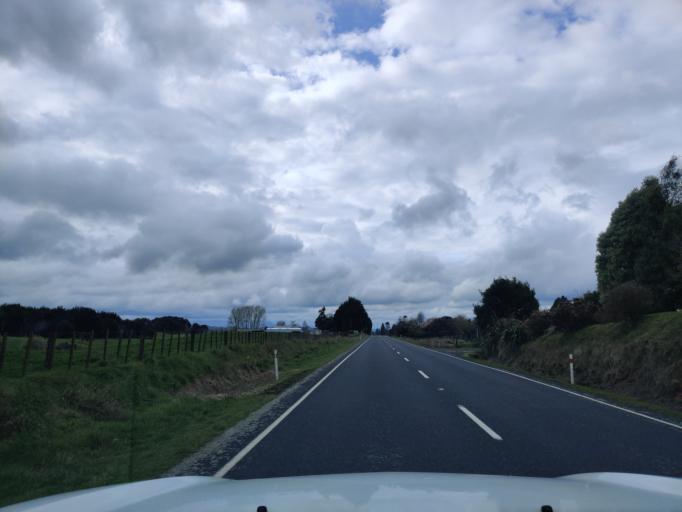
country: NZ
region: Waikato
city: Turangi
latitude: -39.0437
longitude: 175.3833
